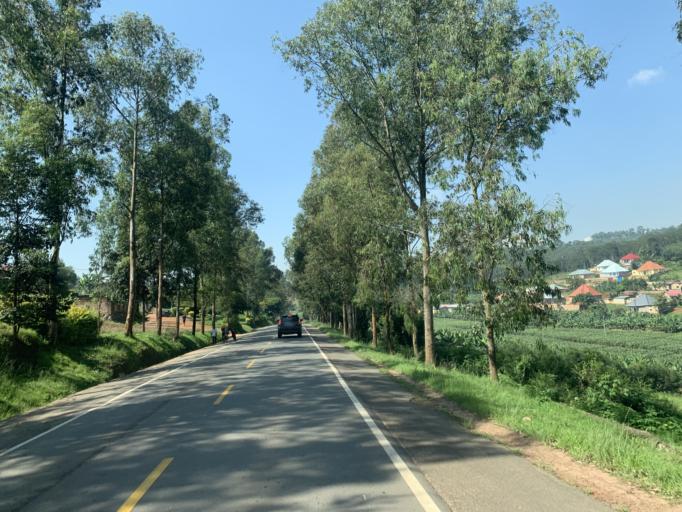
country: RW
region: Kigali
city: Kigali
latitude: -1.9875
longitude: 29.9323
